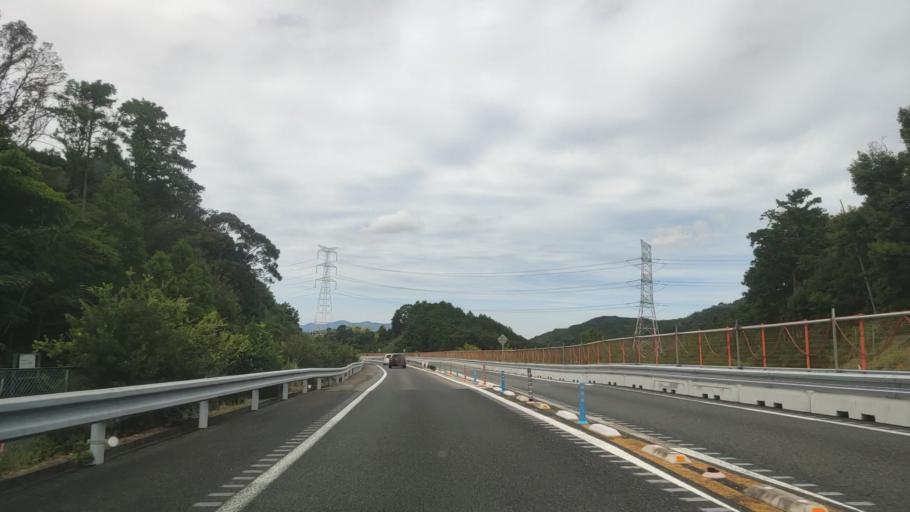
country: JP
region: Wakayama
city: Gobo
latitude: 33.8586
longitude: 135.2083
